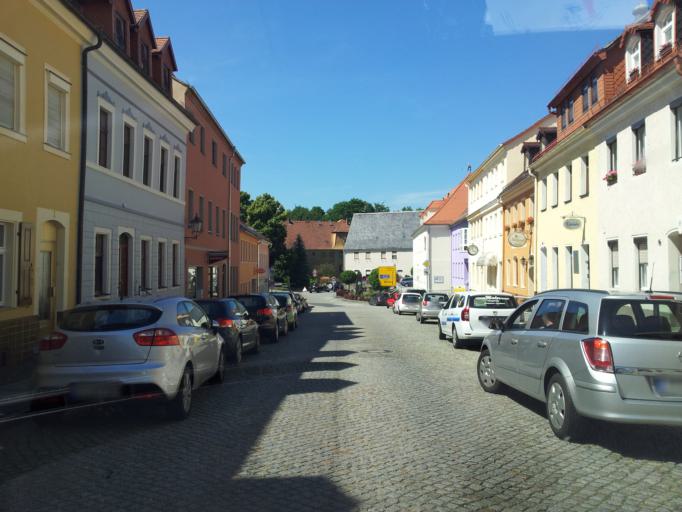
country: DE
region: Saxony
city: Konigsbruck
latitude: 51.2638
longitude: 13.9020
